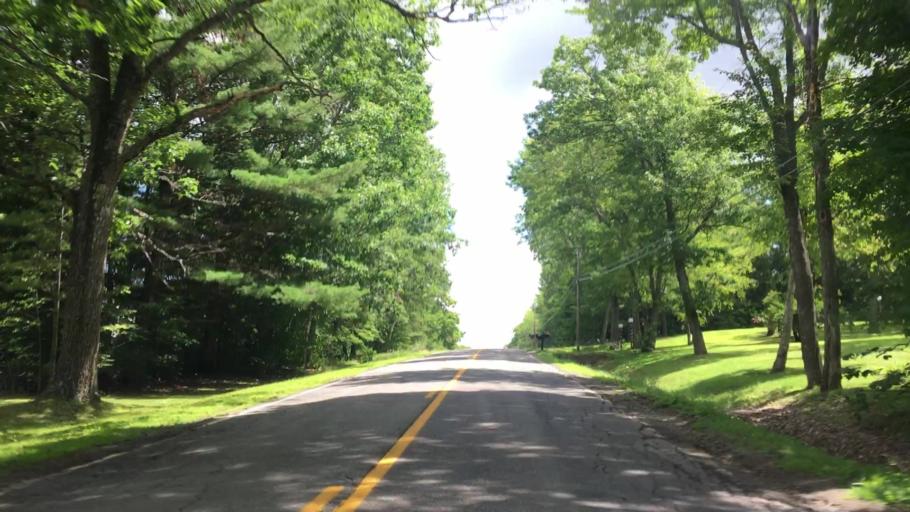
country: US
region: Maine
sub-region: Penobscot County
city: Carmel
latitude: 44.7938
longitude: -69.0747
